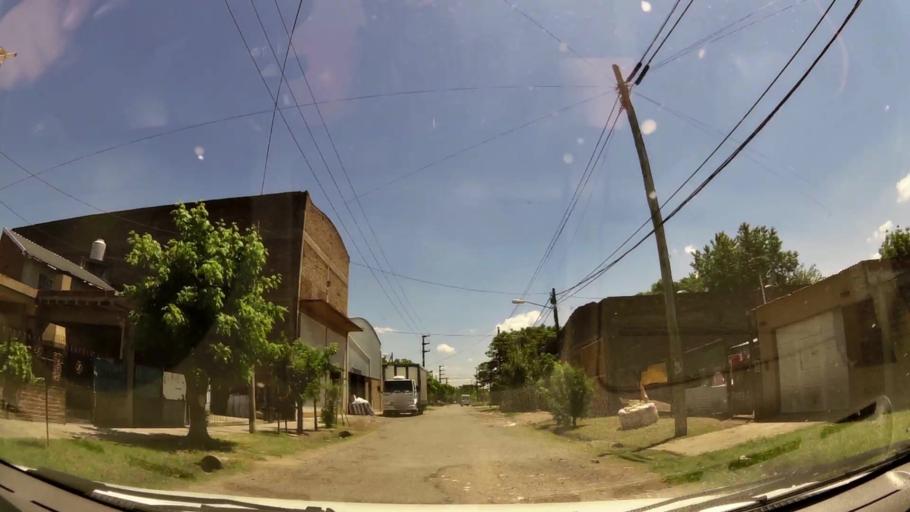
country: AR
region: Buenos Aires
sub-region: Partido de Merlo
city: Merlo
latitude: -34.6436
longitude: -58.7115
